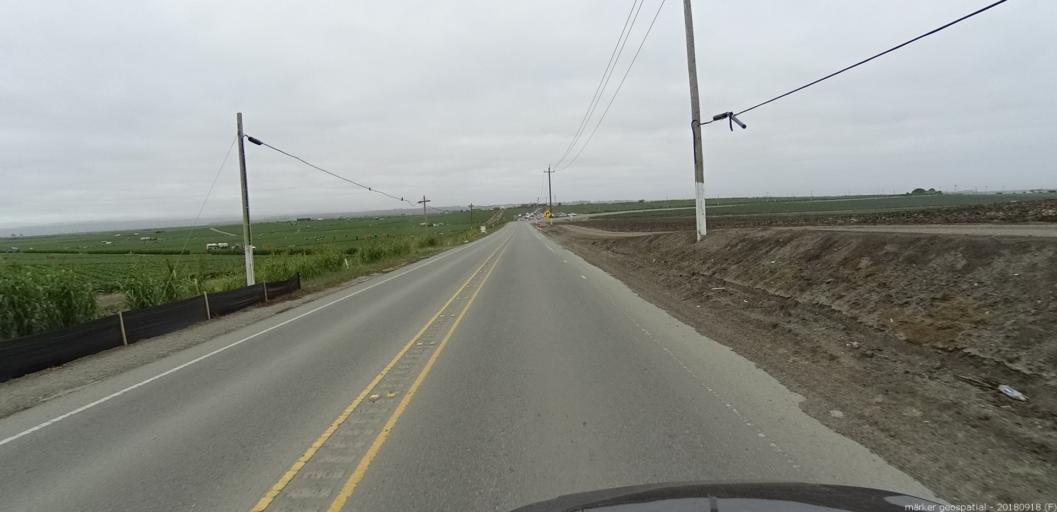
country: US
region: California
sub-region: Monterey County
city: Castroville
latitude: 36.7444
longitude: -121.7291
